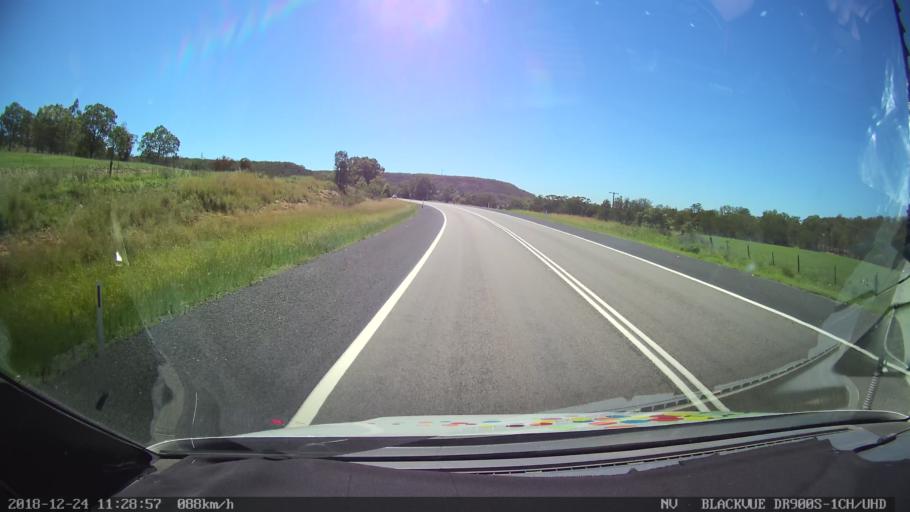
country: AU
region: New South Wales
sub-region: Upper Hunter Shire
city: Merriwa
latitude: -32.1907
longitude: 150.4547
